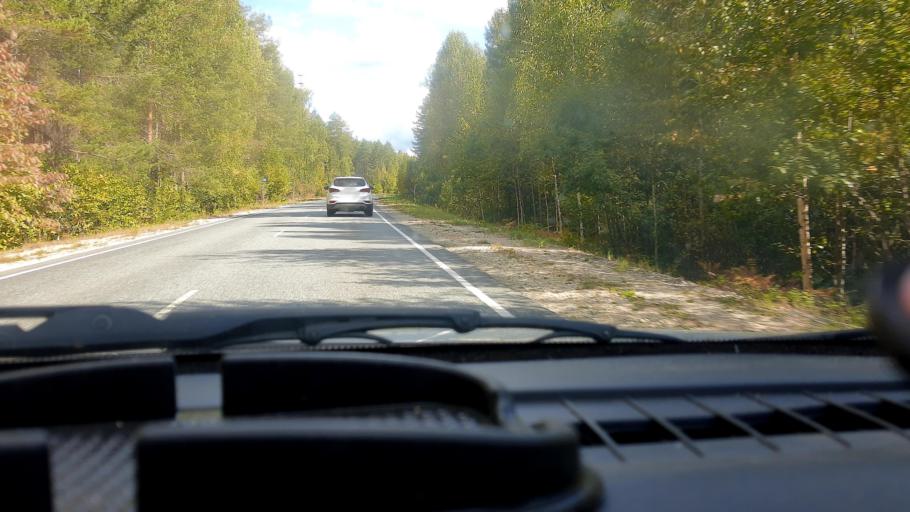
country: RU
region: Kirov
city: Sanchursk
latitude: 56.5824
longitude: 47.2186
